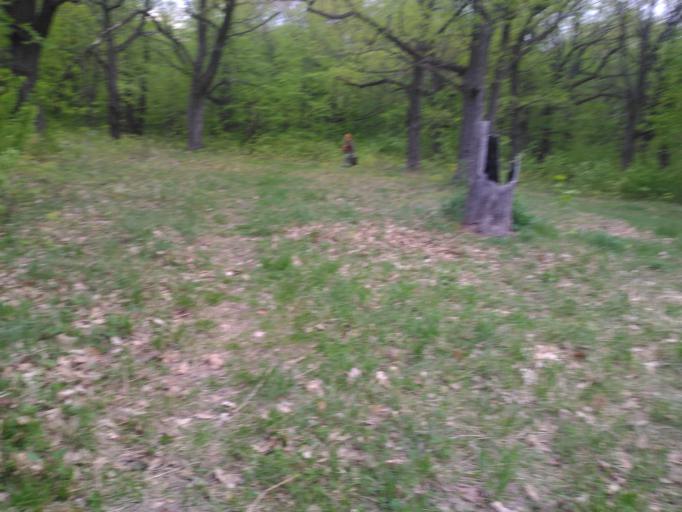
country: RU
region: Ulyanovsk
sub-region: Ulyanovskiy Rayon
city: Ulyanovsk
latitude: 54.2736
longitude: 48.3519
